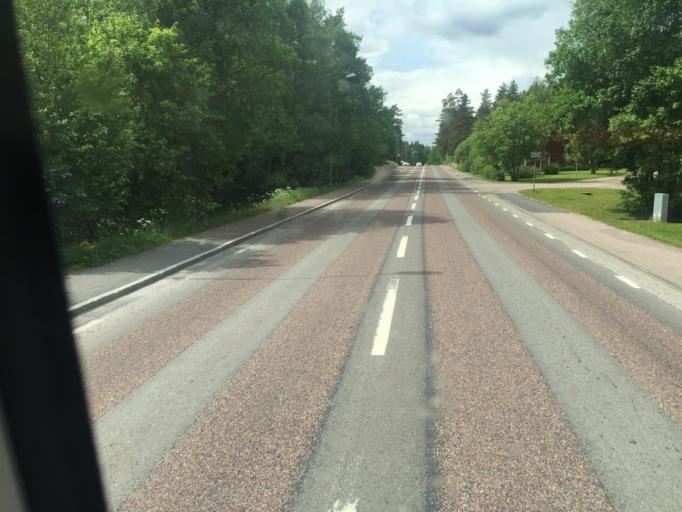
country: SE
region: Dalarna
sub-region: Vansbro Kommun
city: Vansbro
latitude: 60.5099
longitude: 14.2120
